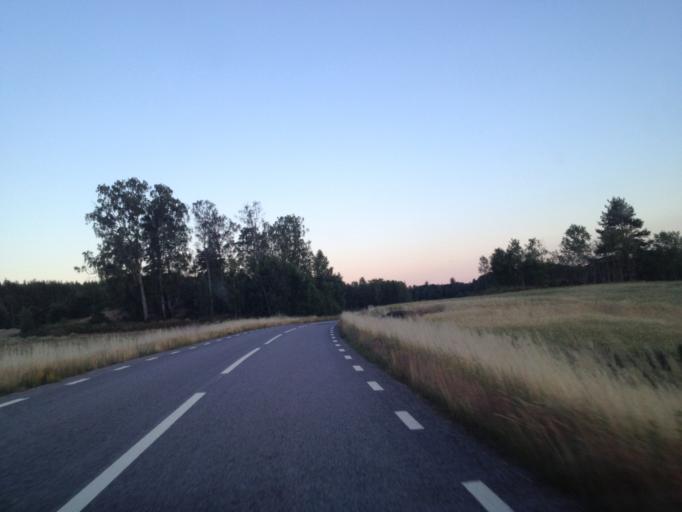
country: SE
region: Kalmar
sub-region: Vasterviks Kommun
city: Overum
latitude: 58.0001
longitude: 16.1777
